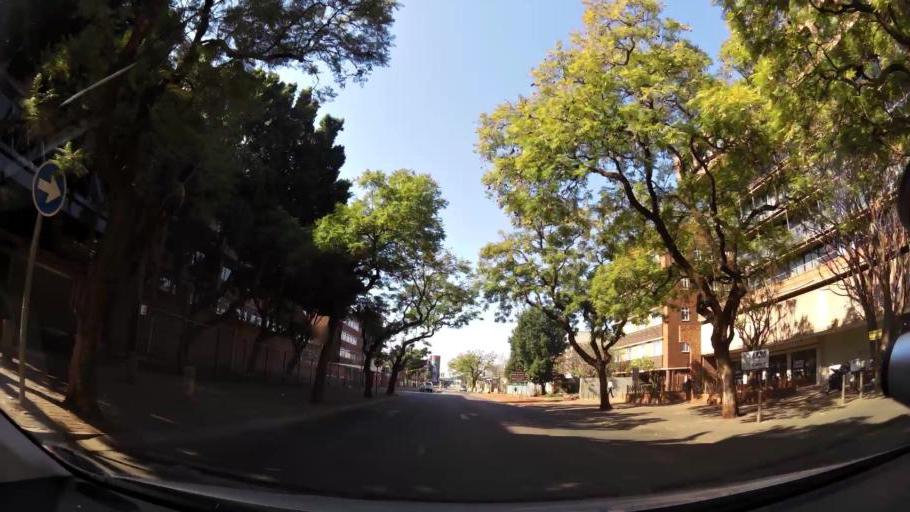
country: ZA
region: Gauteng
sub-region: City of Tshwane Metropolitan Municipality
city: Pretoria
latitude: -25.7477
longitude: 28.2337
